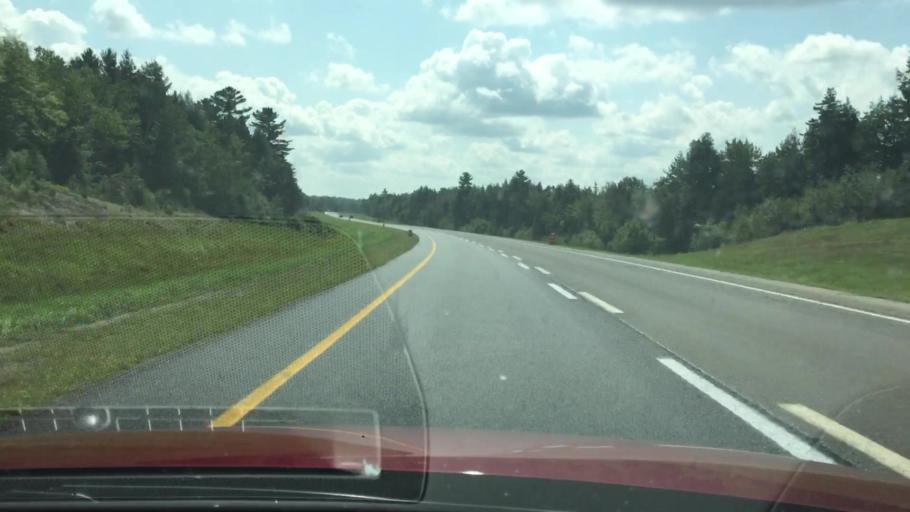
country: US
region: Maine
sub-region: Penobscot County
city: Medway
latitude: 45.6992
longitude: -68.4862
